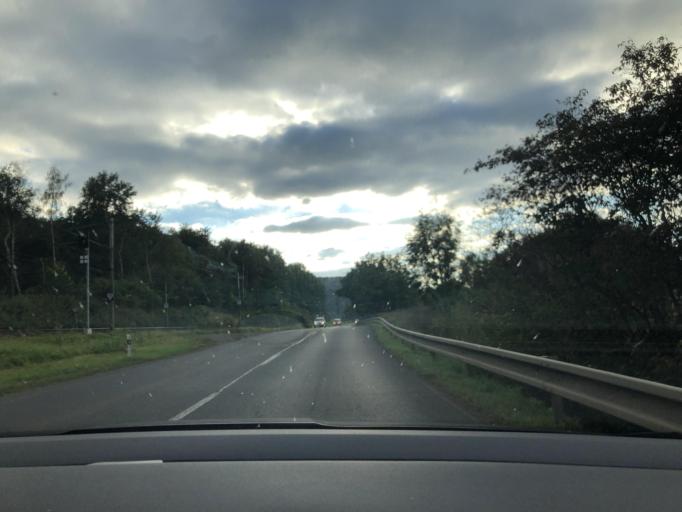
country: CZ
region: Ustecky
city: Velke Brezno
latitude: 50.6692
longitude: 14.1163
